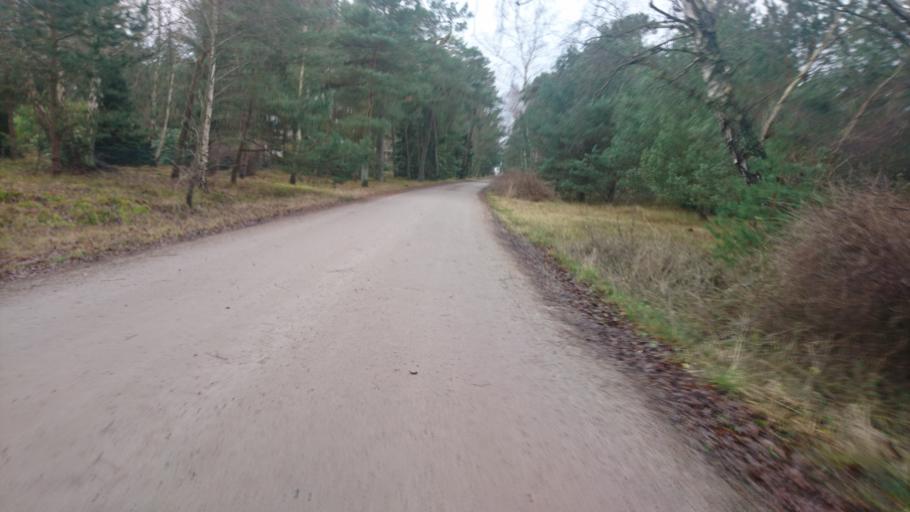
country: SE
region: Skane
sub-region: Vellinge Kommun
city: Ljunghusen
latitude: 55.3897
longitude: 12.9187
